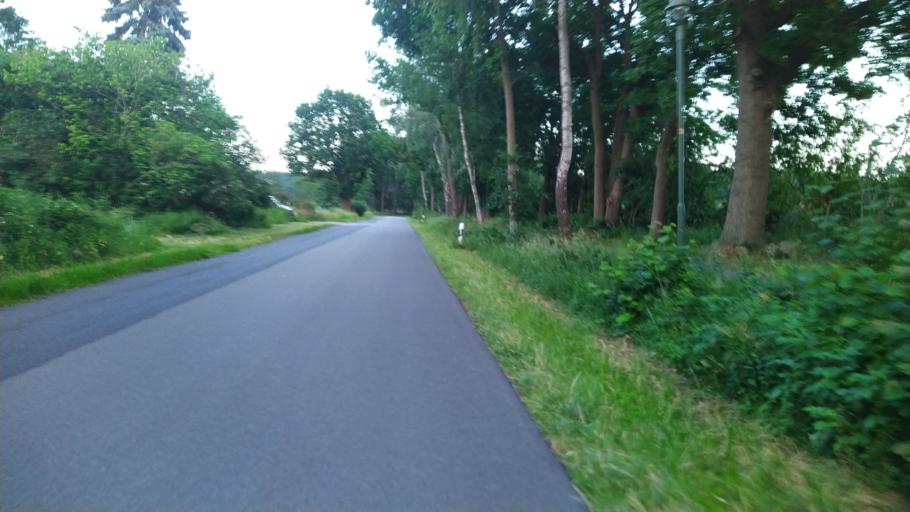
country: DE
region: Lower Saxony
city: Bremervorde
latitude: 53.4852
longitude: 9.1860
